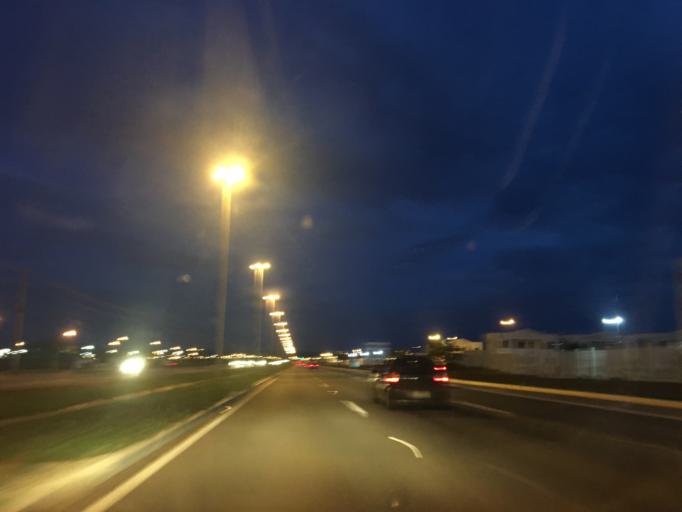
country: BR
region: Federal District
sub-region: Brasilia
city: Brasilia
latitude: -15.8860
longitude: -47.8140
